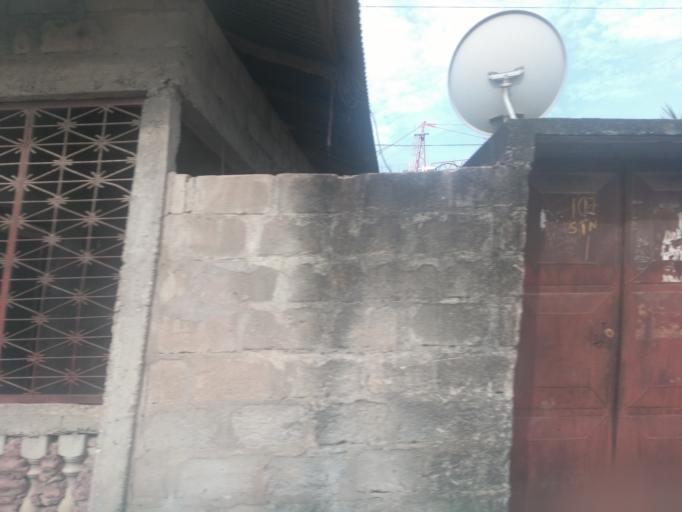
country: TZ
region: Zanzibar Urban/West
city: Zanzibar
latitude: -6.1551
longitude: 39.2088
